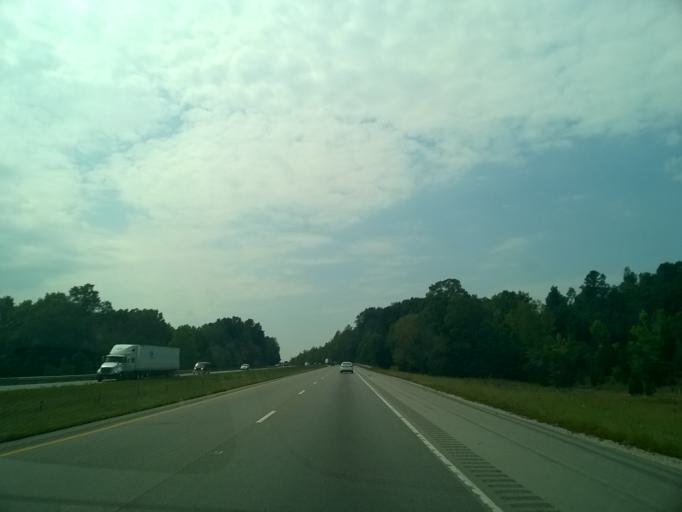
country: US
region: Indiana
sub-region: Clay County
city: Brazil
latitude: 39.4994
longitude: -86.9719
